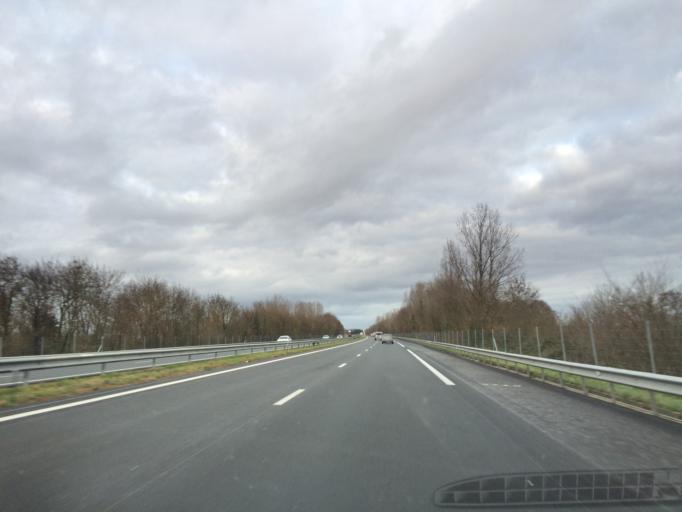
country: FR
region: Poitou-Charentes
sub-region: Departement des Deux-Sevres
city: Aiffres
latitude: 46.2753
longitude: -0.4025
